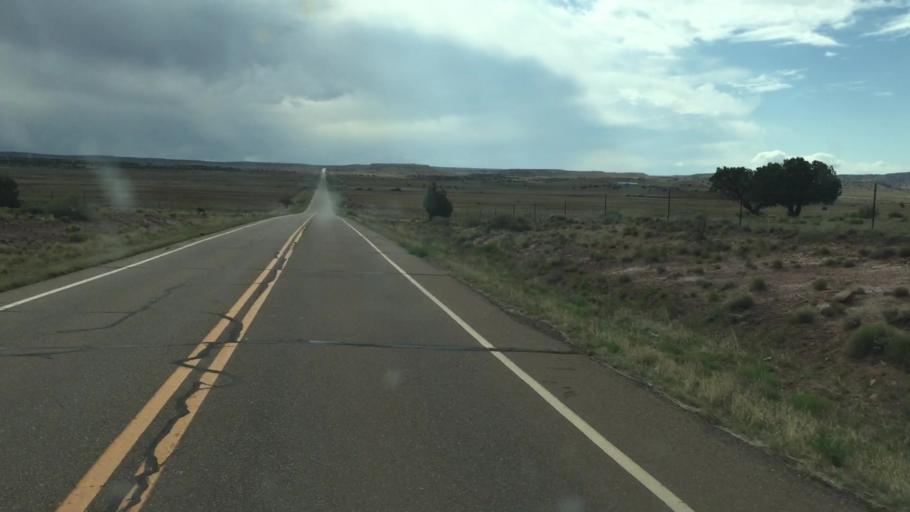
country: US
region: Arizona
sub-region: Apache County
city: Saint Johns
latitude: 34.5103
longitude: -109.6845
